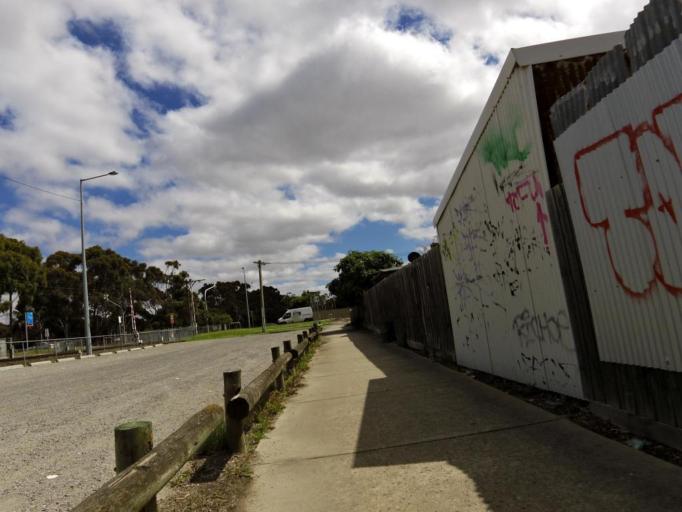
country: AU
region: Victoria
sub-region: Moreland
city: Fawkner
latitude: -37.7196
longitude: 144.9614
